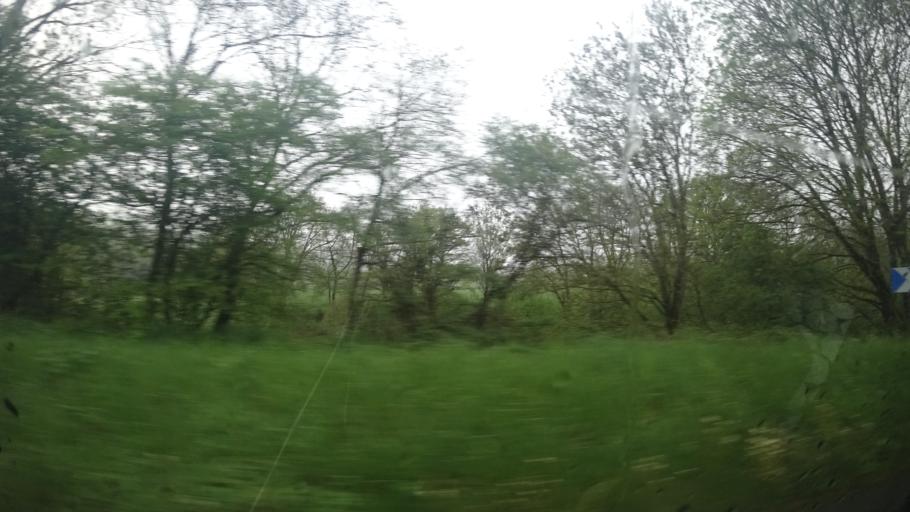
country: FR
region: Midi-Pyrenees
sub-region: Departement de l'Aveyron
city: Laissac
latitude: 44.3131
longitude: 2.8017
